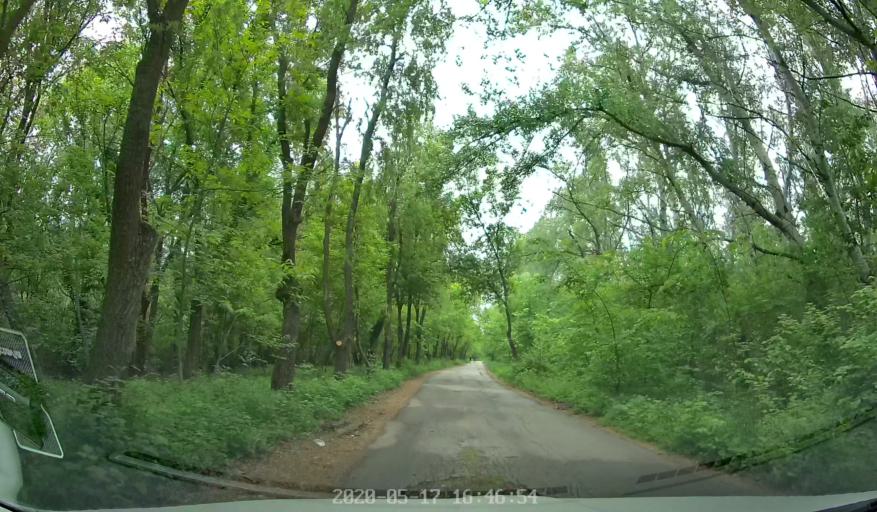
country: MD
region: Chisinau
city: Vatra
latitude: 47.0522
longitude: 28.7855
